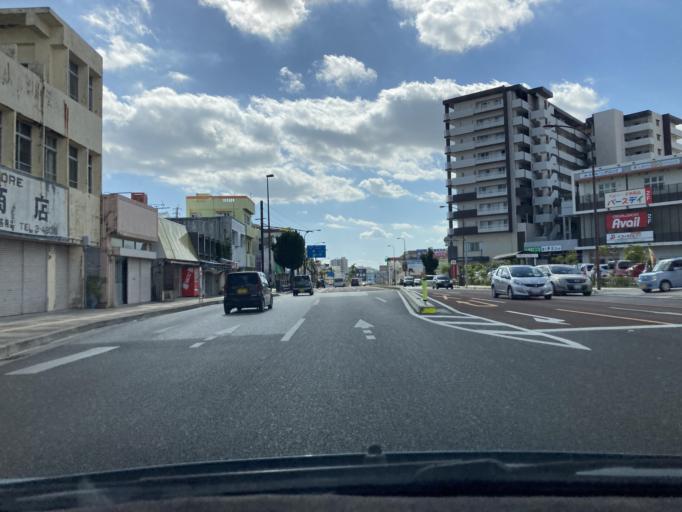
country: JP
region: Okinawa
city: Okinawa
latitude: 26.3247
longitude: 127.7930
